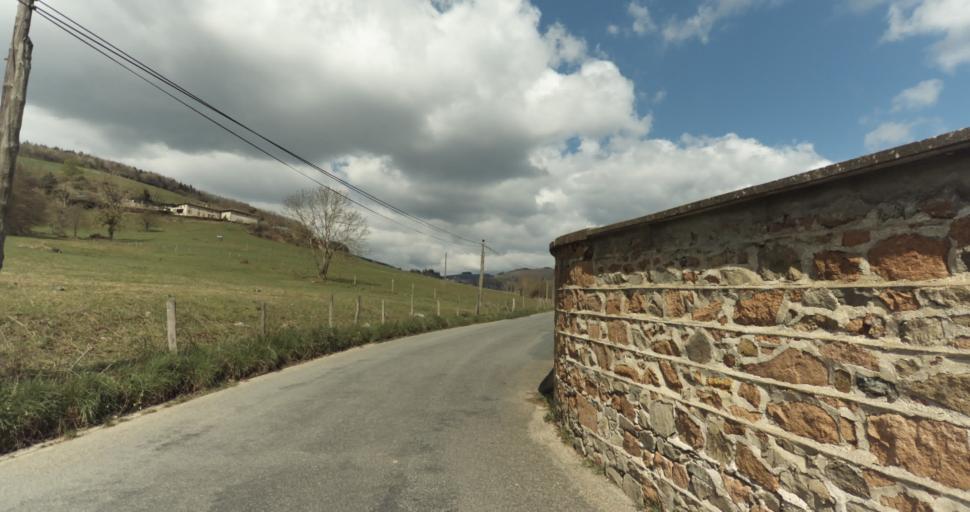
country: FR
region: Rhone-Alpes
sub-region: Departement du Rhone
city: Tarare
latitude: 45.9062
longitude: 4.4284
